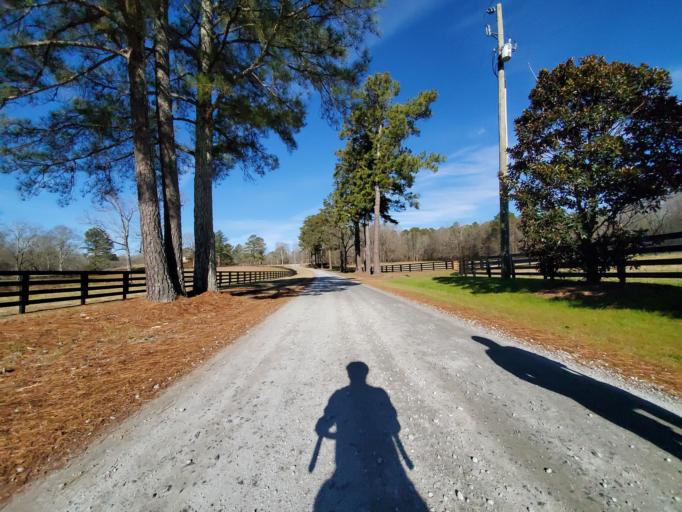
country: US
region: Georgia
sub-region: Fulton County
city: Chattahoochee Hills
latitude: 33.5498
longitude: -84.7945
